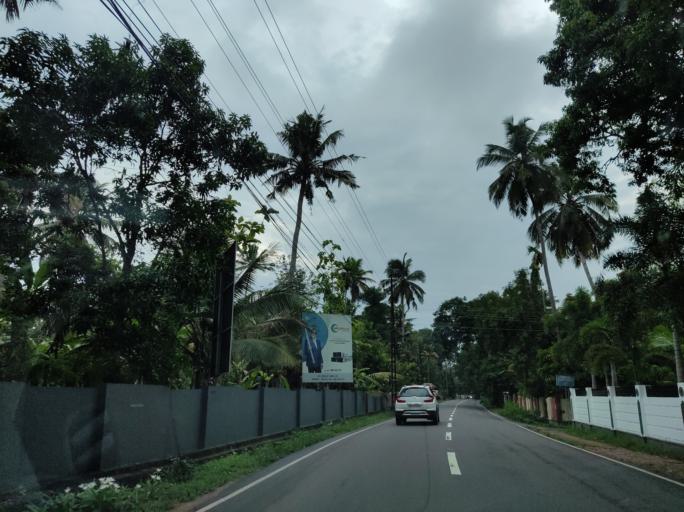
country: IN
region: Kerala
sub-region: Alappuzha
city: Mavelikara
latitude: 9.2519
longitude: 76.5129
